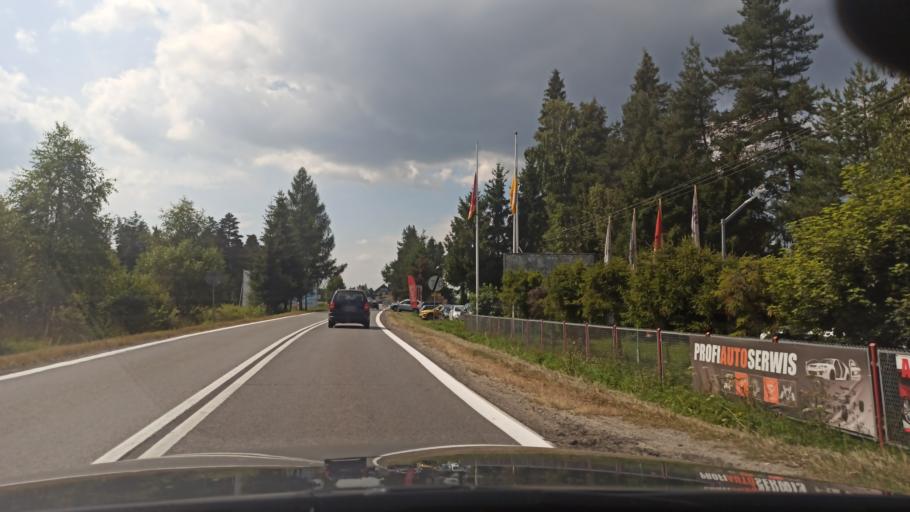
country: PL
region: Lesser Poland Voivodeship
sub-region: Powiat nowotarski
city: Lopuszna
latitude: 49.4701
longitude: 20.1554
